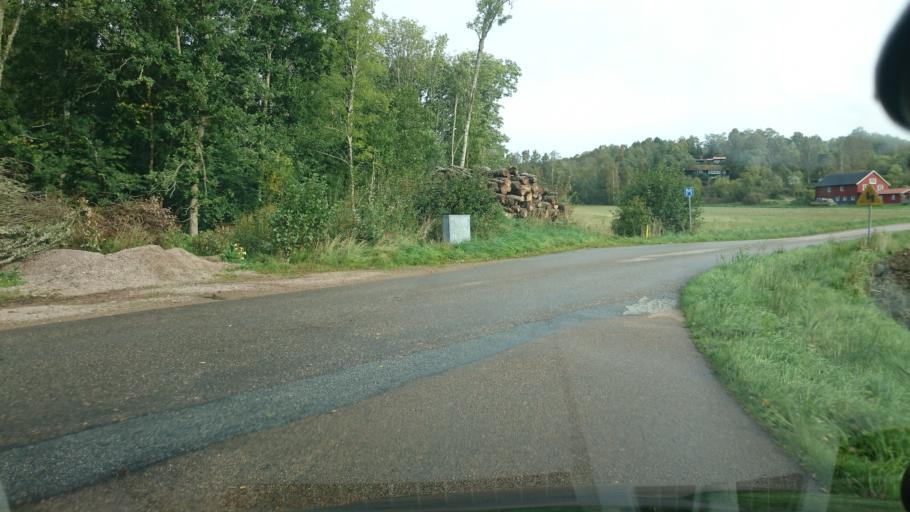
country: SE
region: Vaestra Goetaland
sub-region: Orust
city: Henan
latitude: 58.2660
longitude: 11.5714
